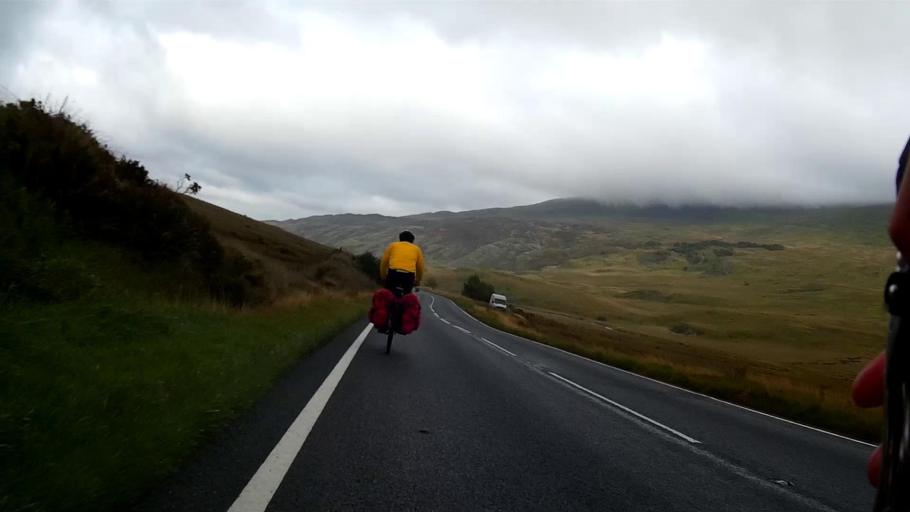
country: GB
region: Wales
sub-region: Gwynedd
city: Blaenau-Ffestiniog
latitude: 53.0885
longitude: -3.9756
